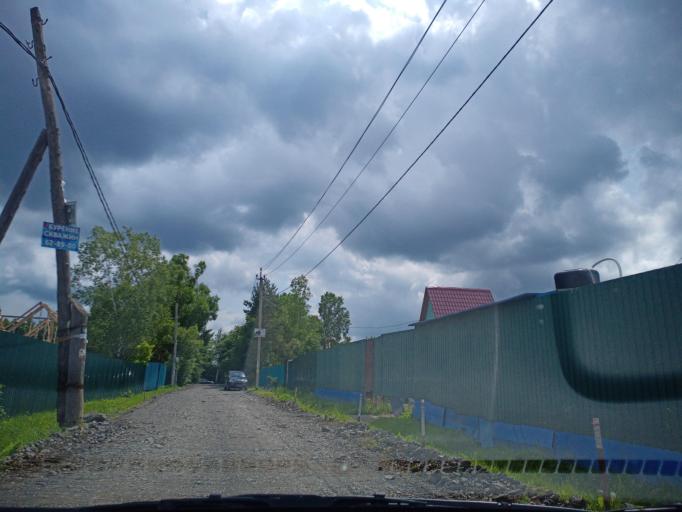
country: RU
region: Khabarovsk Krai
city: Korfovskiy
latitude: 48.3153
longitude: 135.1047
